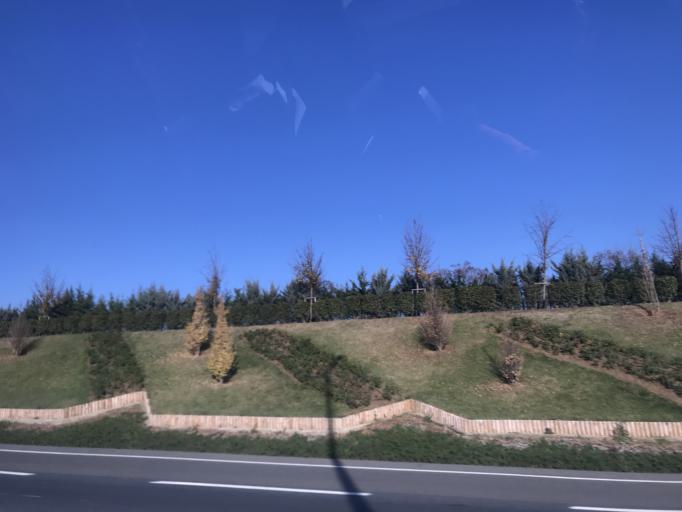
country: TR
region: Istanbul
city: Samandira
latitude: 40.9860
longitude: 29.1975
